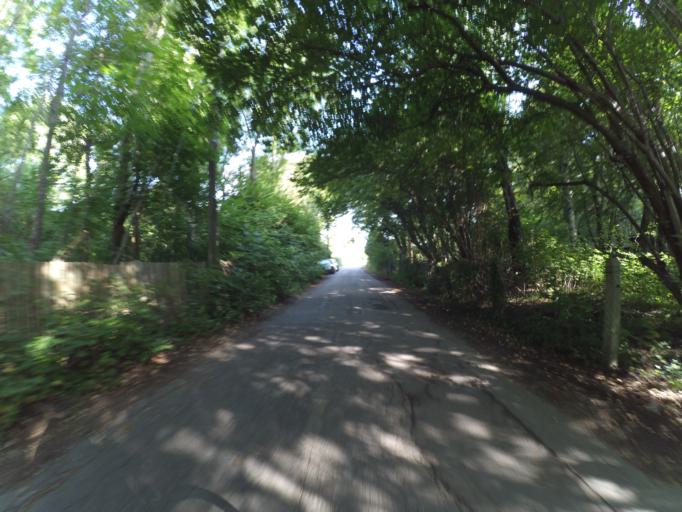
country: DE
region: Bavaria
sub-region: Upper Bavaria
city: Karlsfeld
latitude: 48.1894
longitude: 11.4948
